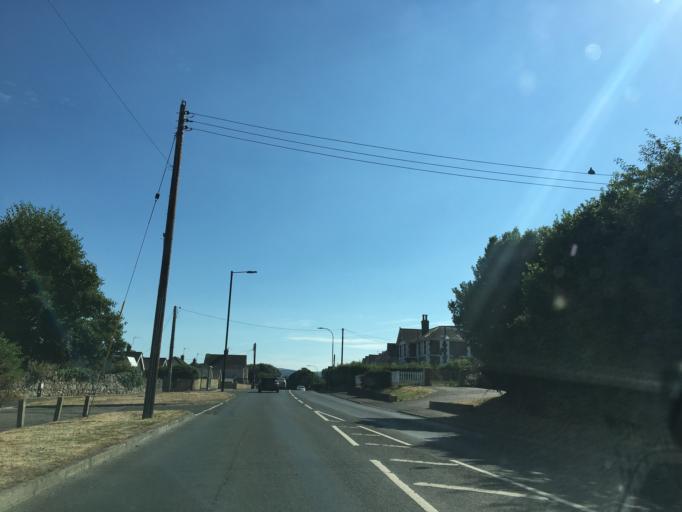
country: GB
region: England
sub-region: Isle of Wight
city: Brading
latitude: 50.6702
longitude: -1.1483
